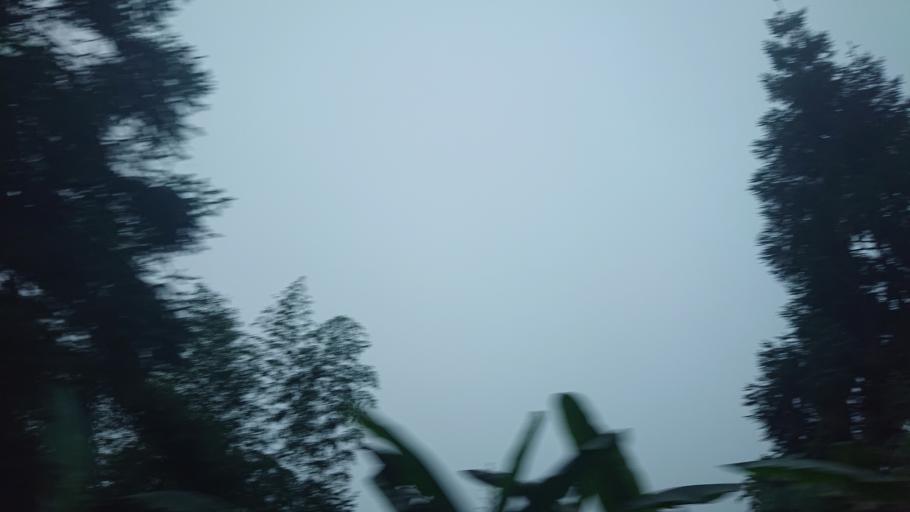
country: TW
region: Taiwan
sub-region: Chiayi
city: Jiayi Shi
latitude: 23.4809
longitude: 120.6963
